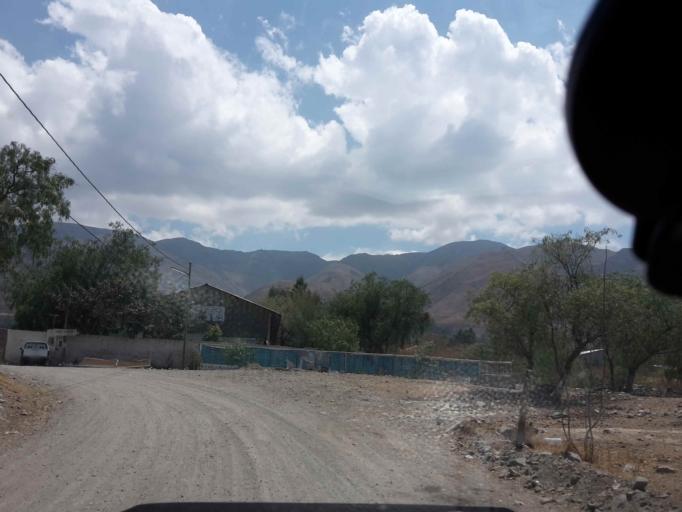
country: BO
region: Cochabamba
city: Cochabamba
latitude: -17.3372
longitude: -66.2114
